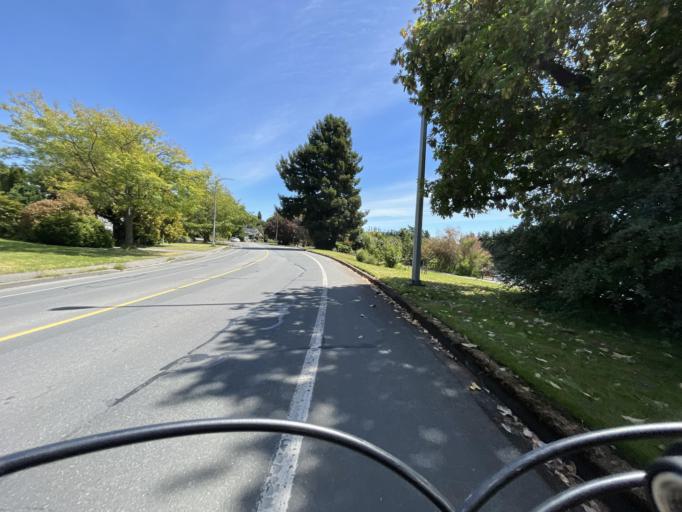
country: CA
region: British Columbia
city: Victoria
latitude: 48.4492
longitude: -123.4072
